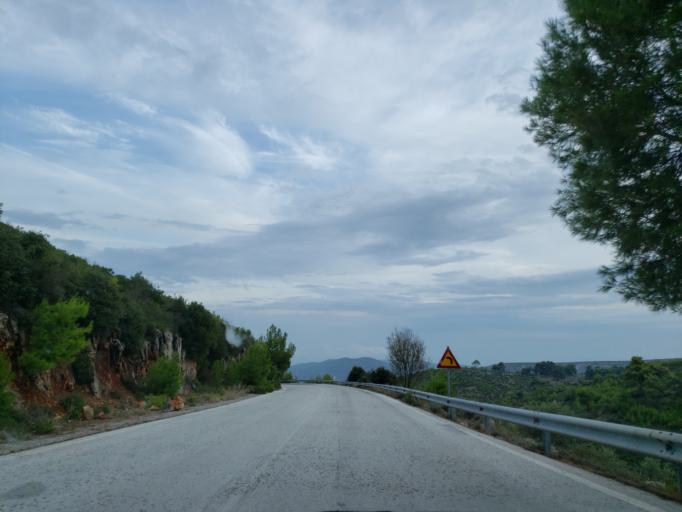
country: GR
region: Attica
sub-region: Nomarchia Anatolikis Attikis
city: Grammatiko
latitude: 38.2114
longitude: 23.9437
